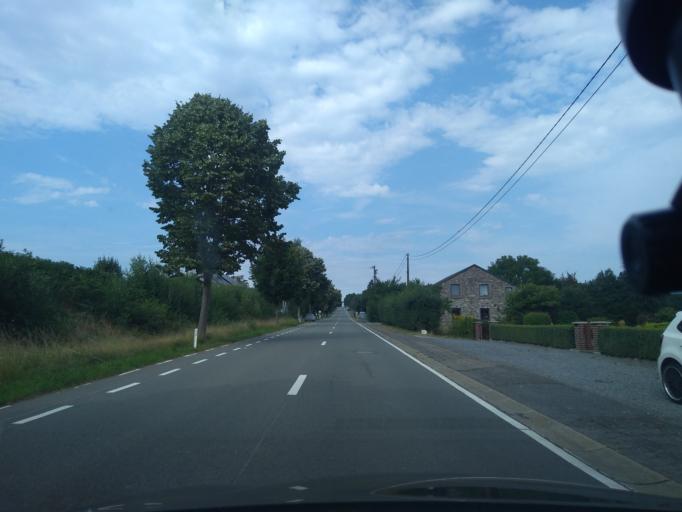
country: BE
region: Wallonia
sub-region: Province du Luxembourg
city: Libin
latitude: 49.9889
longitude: 5.2622
